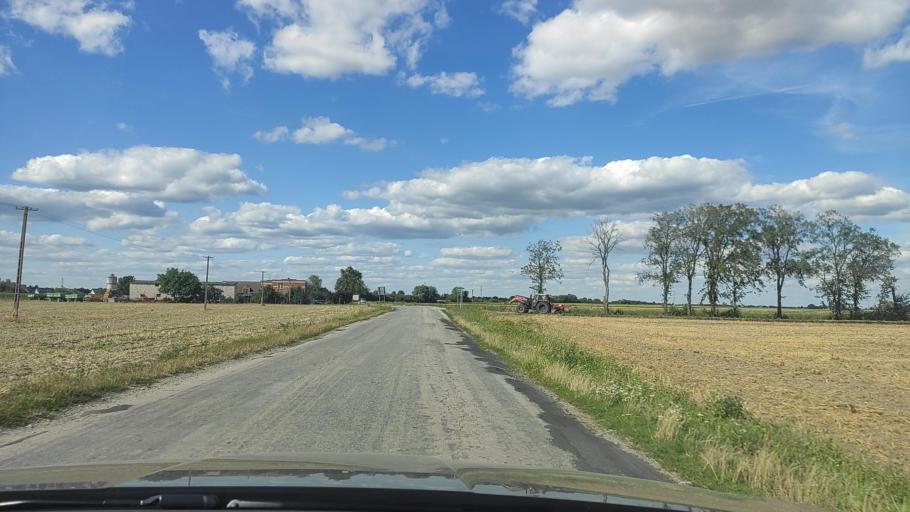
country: PL
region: Greater Poland Voivodeship
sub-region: Powiat poznanski
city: Kleszczewo
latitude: 52.3680
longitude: 17.1674
